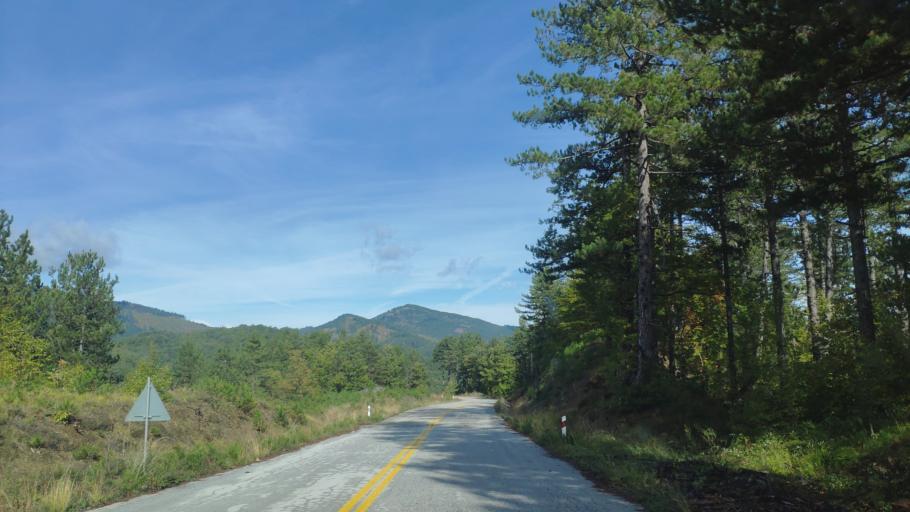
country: GR
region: West Macedonia
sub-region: Nomos Kastorias
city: Nestorio
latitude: 40.3676
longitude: 20.9453
